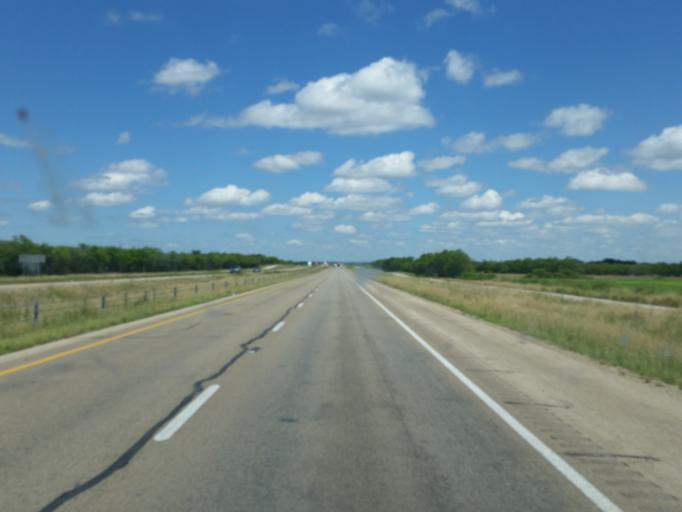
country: US
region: Texas
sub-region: Callahan County
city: Baird
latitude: 32.3877
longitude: -99.3142
